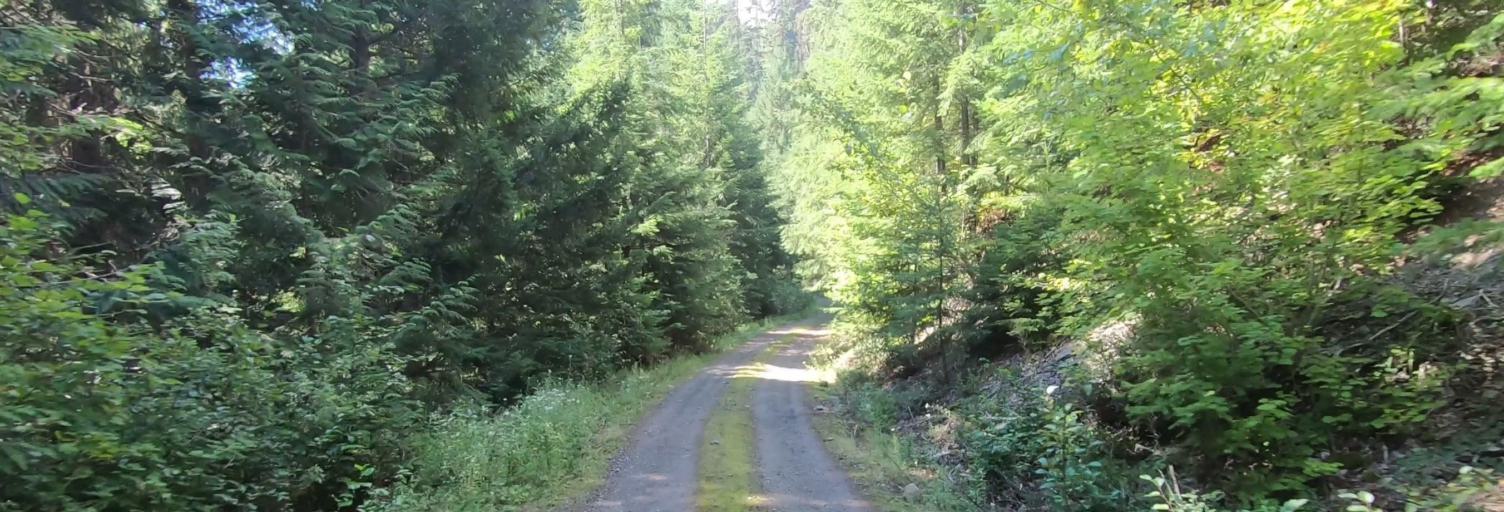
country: CA
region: British Columbia
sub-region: Fraser Valley Regional District
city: Chilliwack
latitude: 48.8678
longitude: -121.7768
